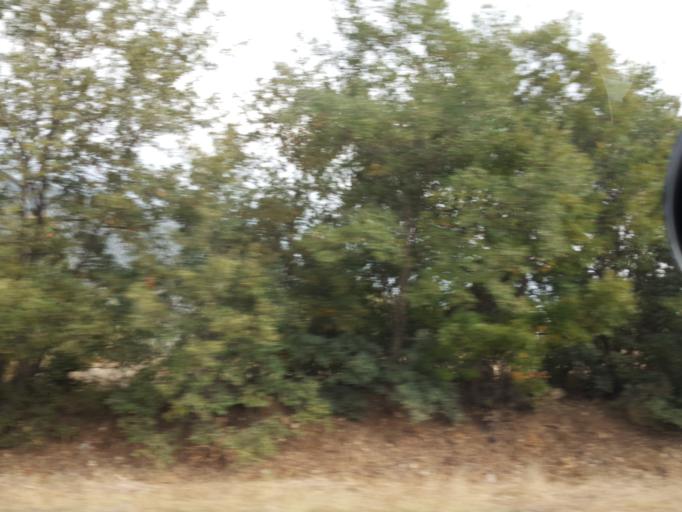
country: TR
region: Amasya
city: Gediksaray
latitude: 40.4803
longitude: 35.7777
